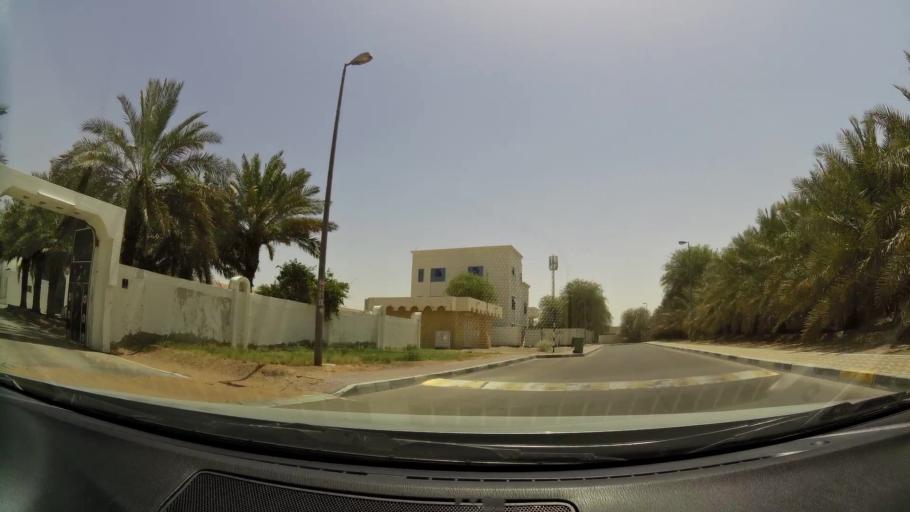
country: OM
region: Al Buraimi
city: Al Buraymi
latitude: 24.2840
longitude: 55.7597
